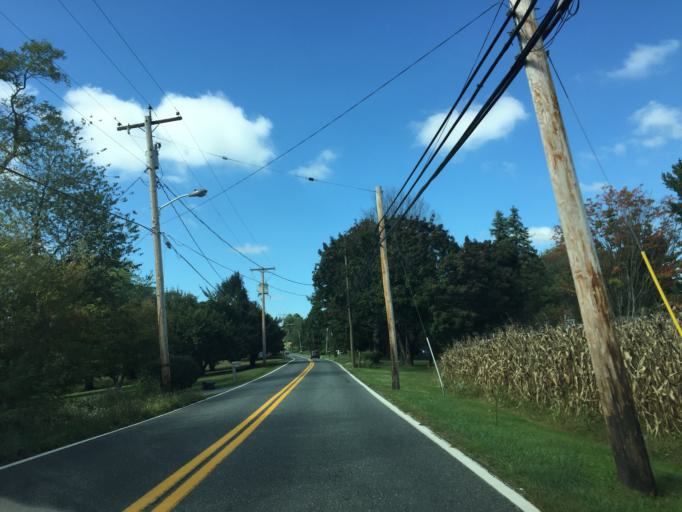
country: US
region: Maryland
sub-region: Harford County
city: Fallston
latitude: 39.4863
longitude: -76.4543
